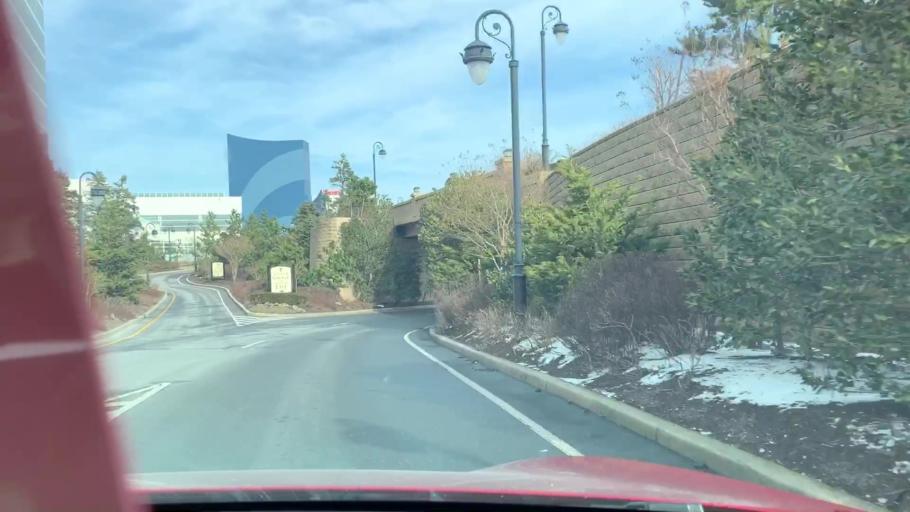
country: US
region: New Jersey
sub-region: Atlantic County
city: Atlantic City
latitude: 39.3775
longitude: -74.4334
